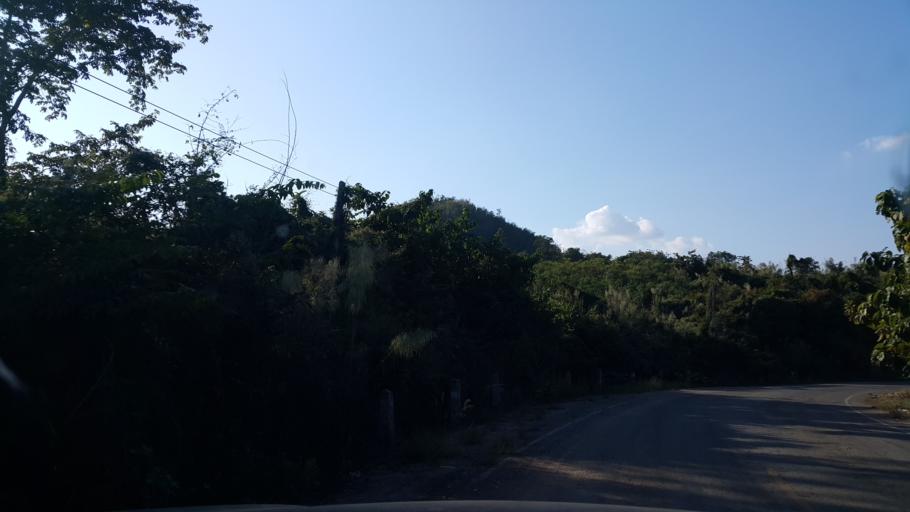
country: TH
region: Sukhothai
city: Thung Saliam
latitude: 17.3889
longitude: 99.5099
